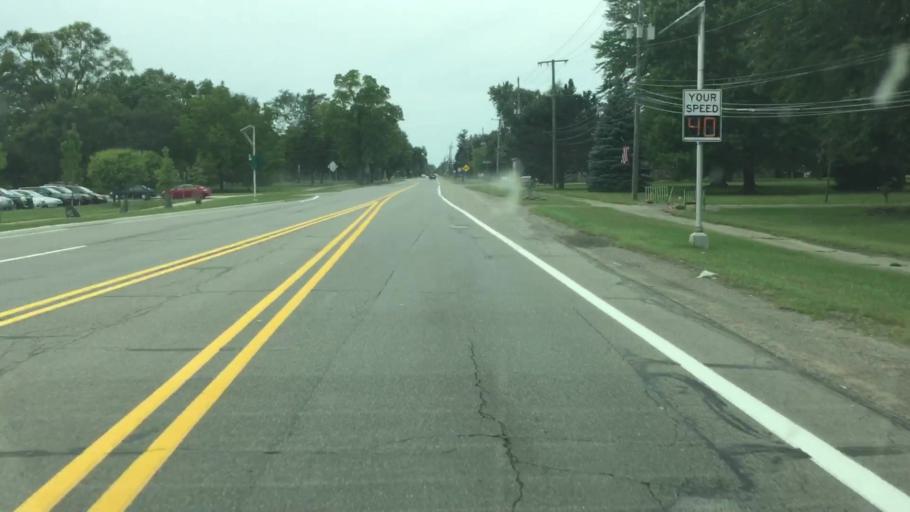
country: US
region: Michigan
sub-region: Oakland County
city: Rochester Hills
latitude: 42.6370
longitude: -83.1028
